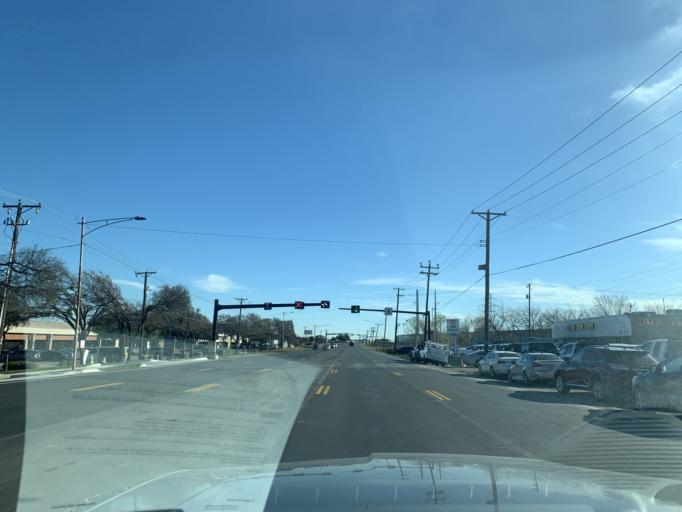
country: US
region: Texas
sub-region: Tarrant County
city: Arlington
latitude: 32.7425
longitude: -97.0779
